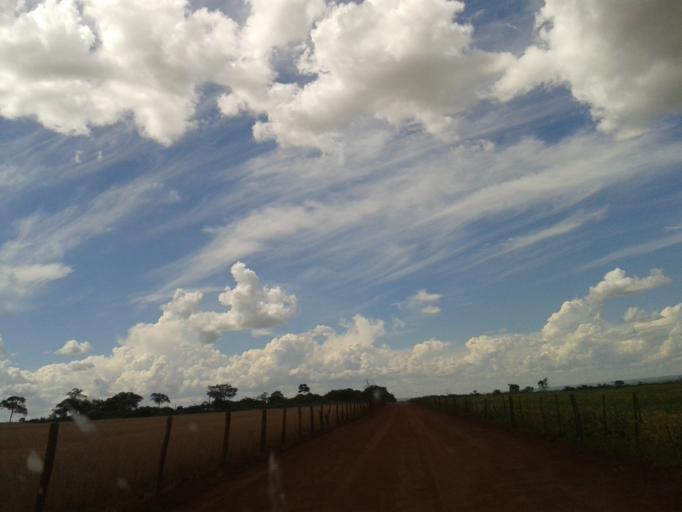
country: BR
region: Minas Gerais
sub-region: Capinopolis
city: Capinopolis
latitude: -18.7147
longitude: -49.7712
